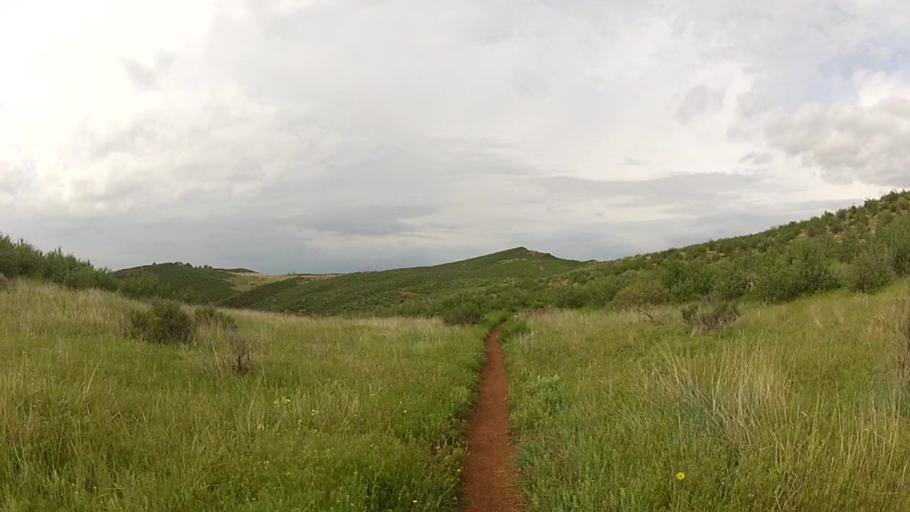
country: US
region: Colorado
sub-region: Larimer County
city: Loveland
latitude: 40.4416
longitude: -105.1541
